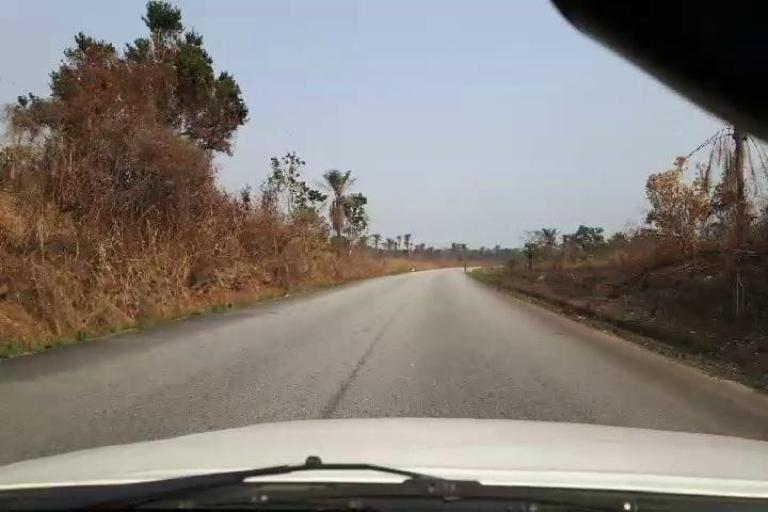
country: SL
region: Southern Province
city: Baiima
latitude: 8.1400
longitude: -11.8984
